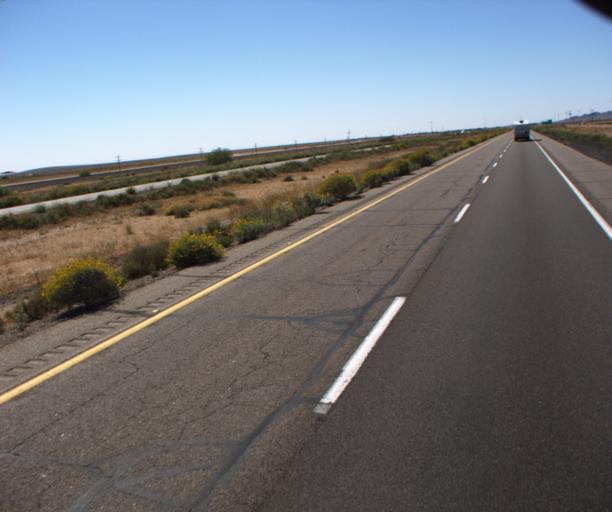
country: US
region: Arizona
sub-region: Maricopa County
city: Gila Bend
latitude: 32.9151
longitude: -112.9334
